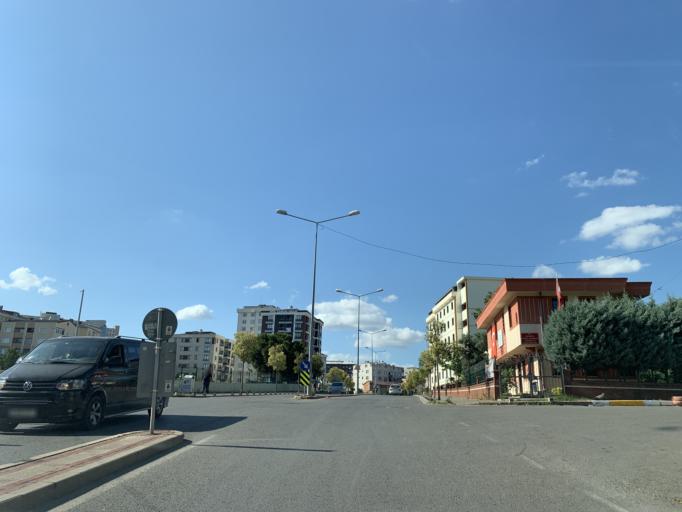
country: TR
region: Istanbul
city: Pendik
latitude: 40.8818
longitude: 29.2671
